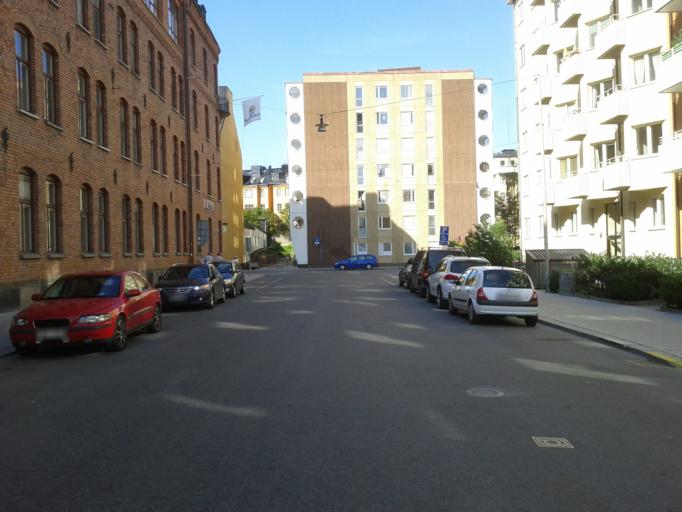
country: SE
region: Stockholm
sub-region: Stockholms Kommun
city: Stockholm
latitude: 59.3353
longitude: 18.0289
